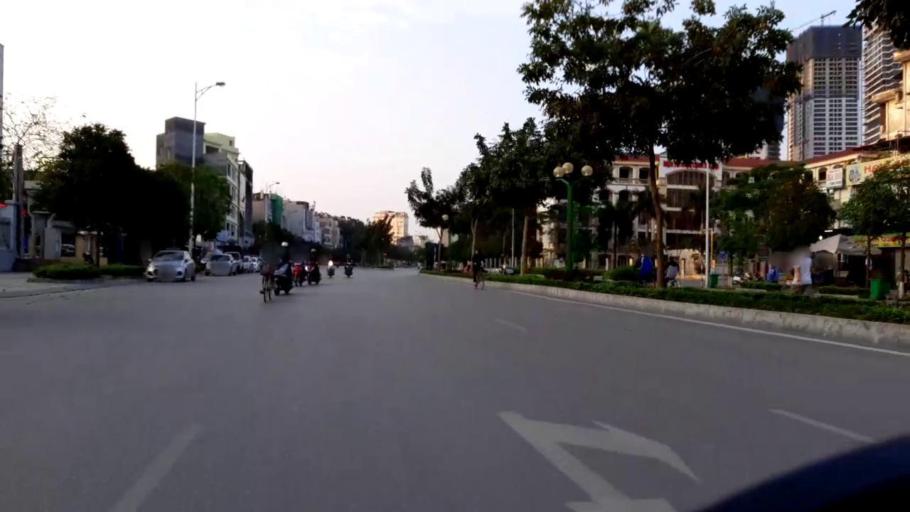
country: VN
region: Ha Noi
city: Cau Giay
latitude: 21.0384
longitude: 105.7978
